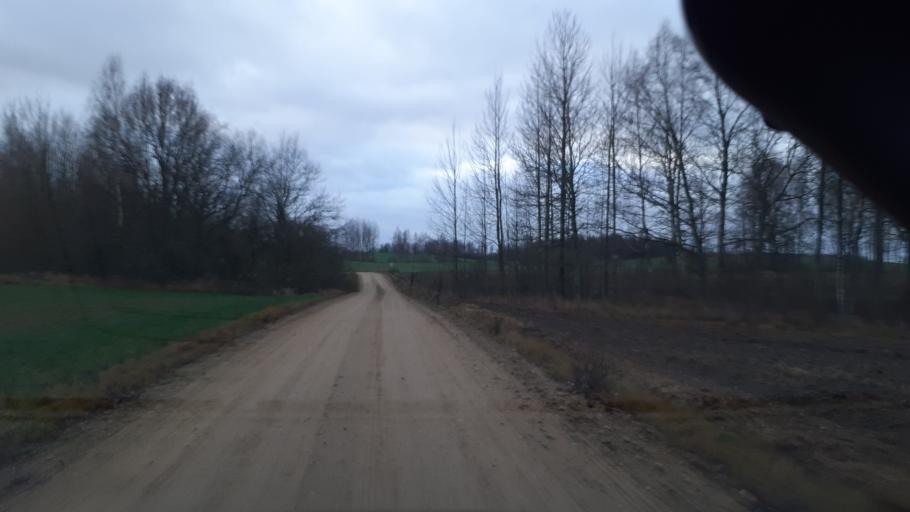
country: LV
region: Kuldigas Rajons
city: Kuldiga
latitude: 56.8722
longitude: 21.7713
